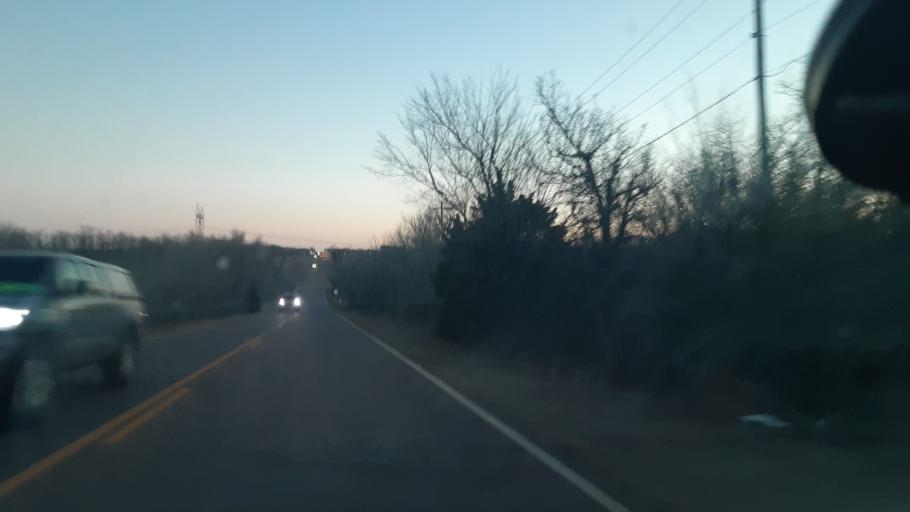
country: US
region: Oklahoma
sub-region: Oklahoma County
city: Edmond
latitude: 35.6917
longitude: -97.4251
